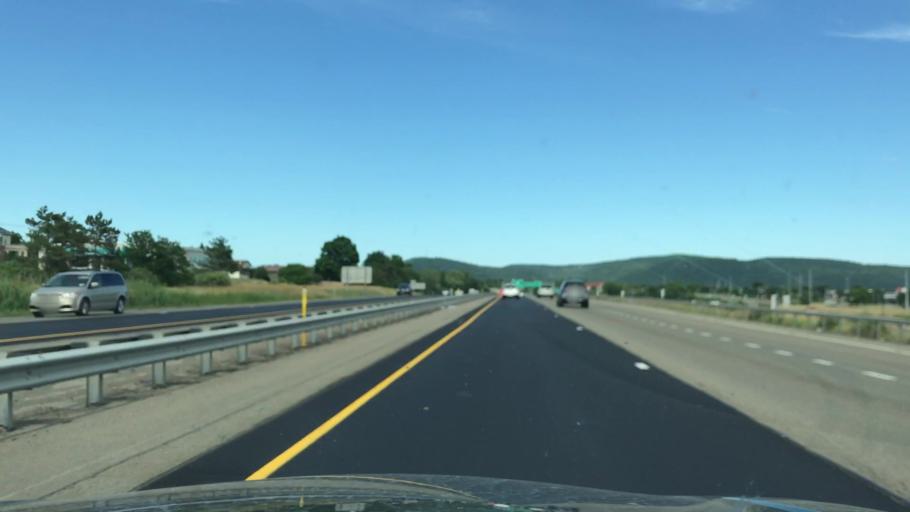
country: US
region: New York
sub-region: Chemung County
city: Horseheads
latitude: 42.1603
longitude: -76.8588
